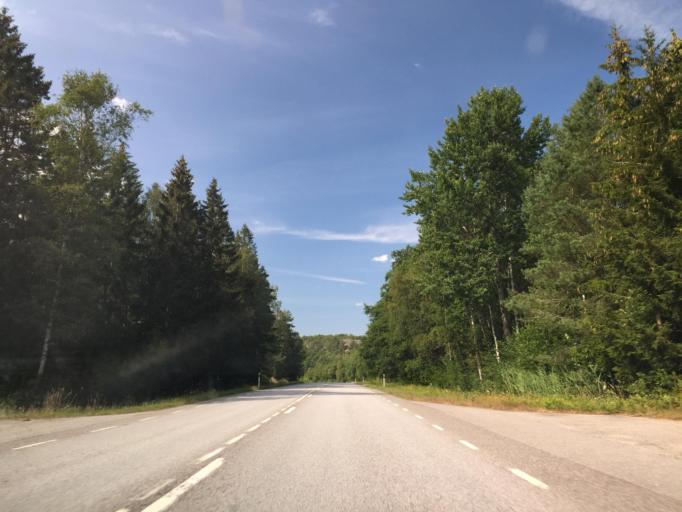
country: SE
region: Vaestra Goetaland
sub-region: Tanums Kommun
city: Tanumshede
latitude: 58.8189
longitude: 11.2617
